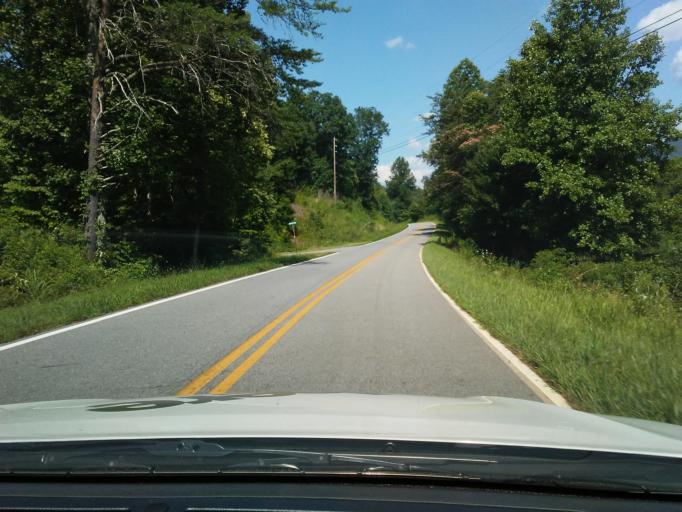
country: US
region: Georgia
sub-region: Union County
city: Blairsville
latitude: 34.9371
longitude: -83.8739
